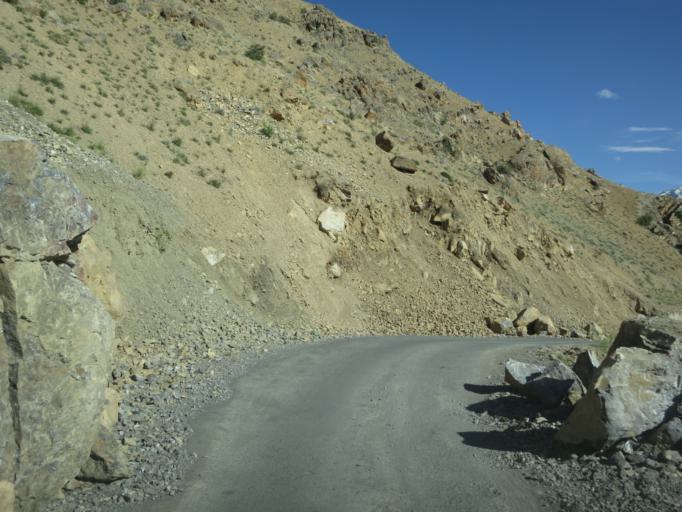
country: IN
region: Himachal Pradesh
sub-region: Shimla
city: Sarahan
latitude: 32.3061
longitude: 78.0045
